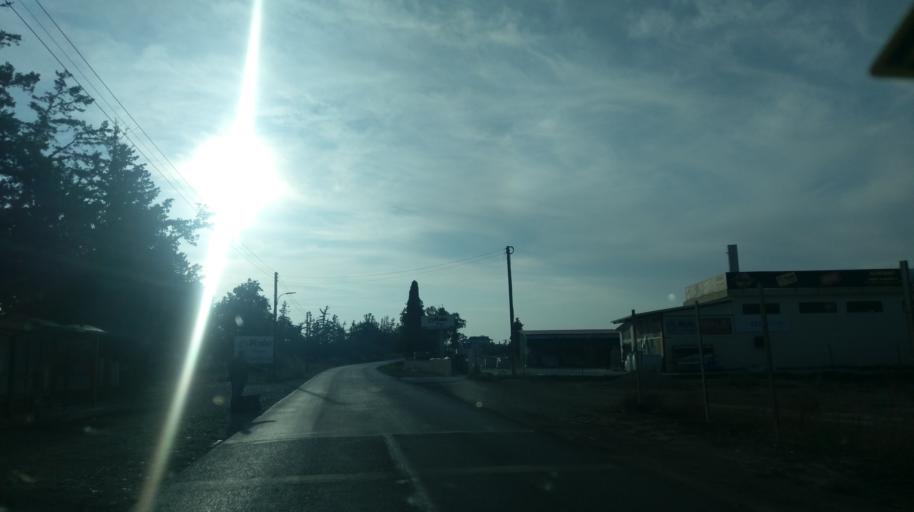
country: CY
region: Larnaka
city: Pergamos
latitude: 35.1098
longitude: 33.7276
